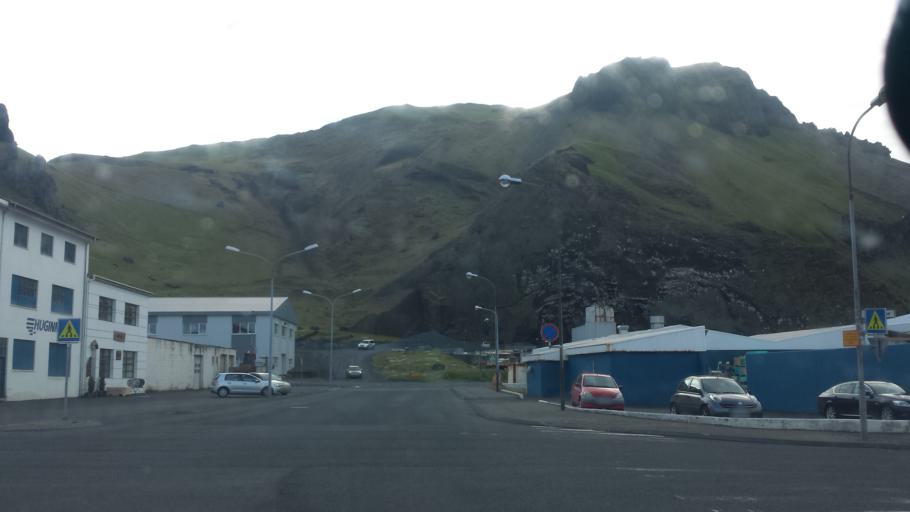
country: IS
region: South
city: Vestmannaeyjar
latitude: 63.4430
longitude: -20.2795
